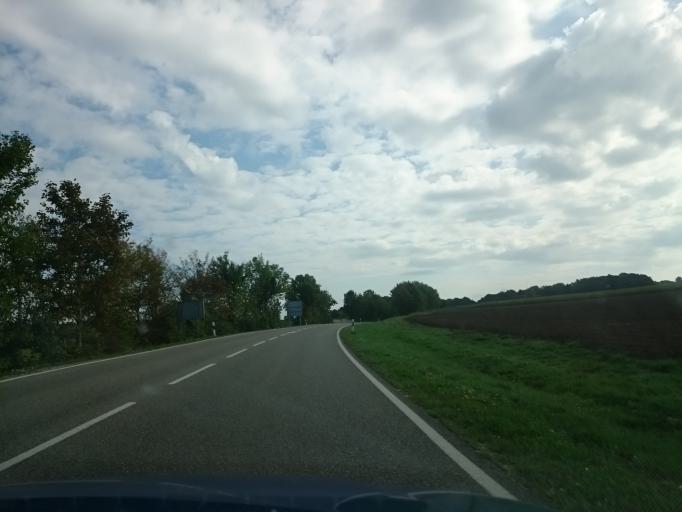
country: DE
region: Bavaria
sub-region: Regierungsbezirk Mittelfranken
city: Hilpoltstein
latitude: 49.2263
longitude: 11.2006
